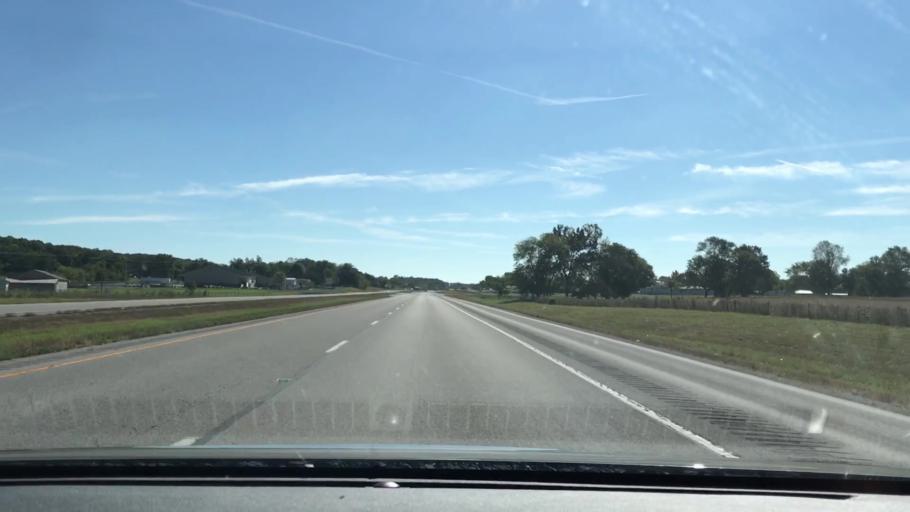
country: US
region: Kentucky
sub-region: Todd County
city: Elkton
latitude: 36.8380
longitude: -87.2412
